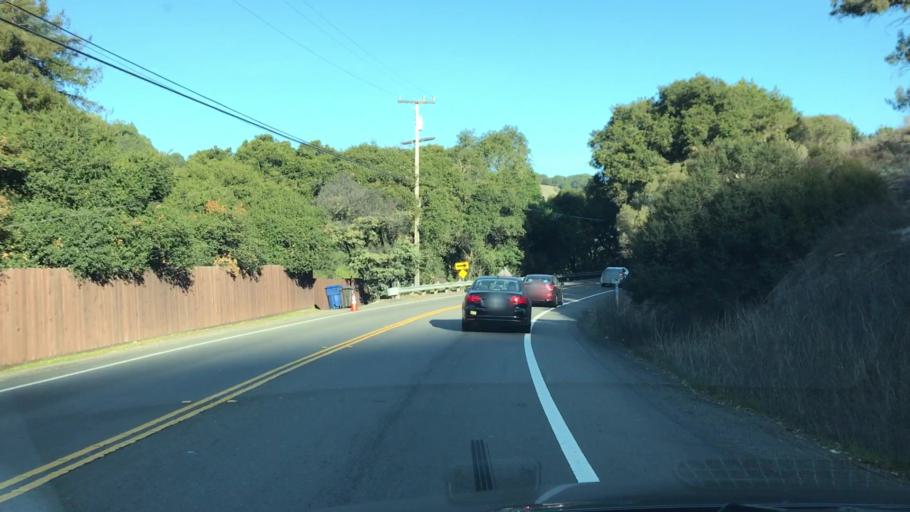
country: US
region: California
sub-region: Alameda County
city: Fairview
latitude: 37.7190
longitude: -122.0382
